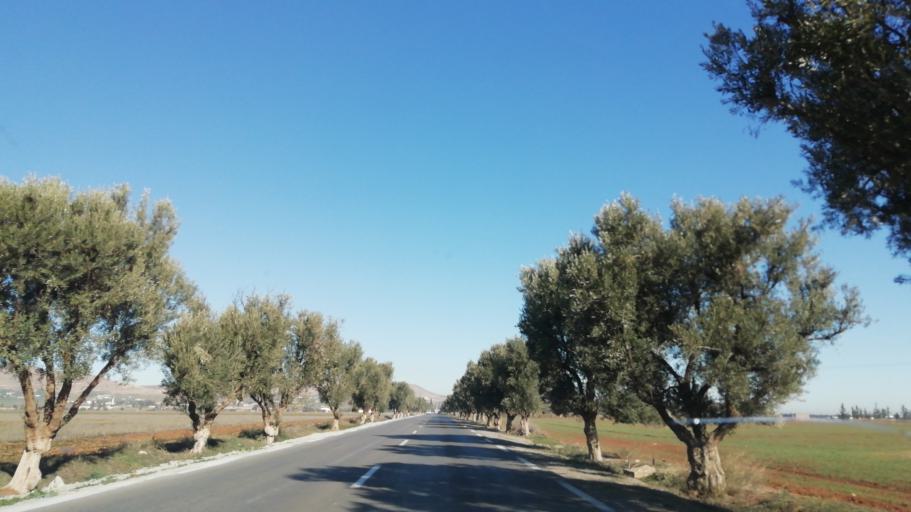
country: DZ
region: Mascara
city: Bou Hanifia el Hamamat
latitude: 35.2042
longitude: 0.1094
